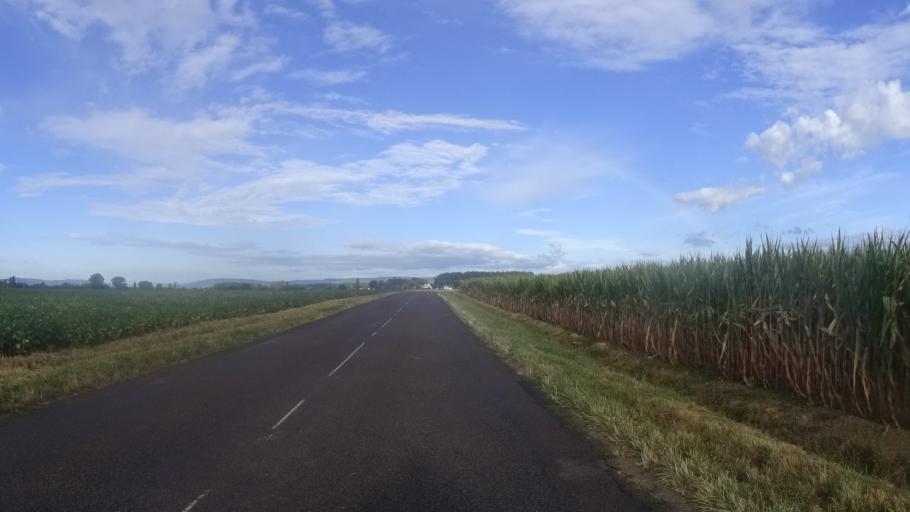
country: FR
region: Bourgogne
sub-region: Departement de Saone-et-Loire
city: Demigny
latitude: 46.9583
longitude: 4.8789
